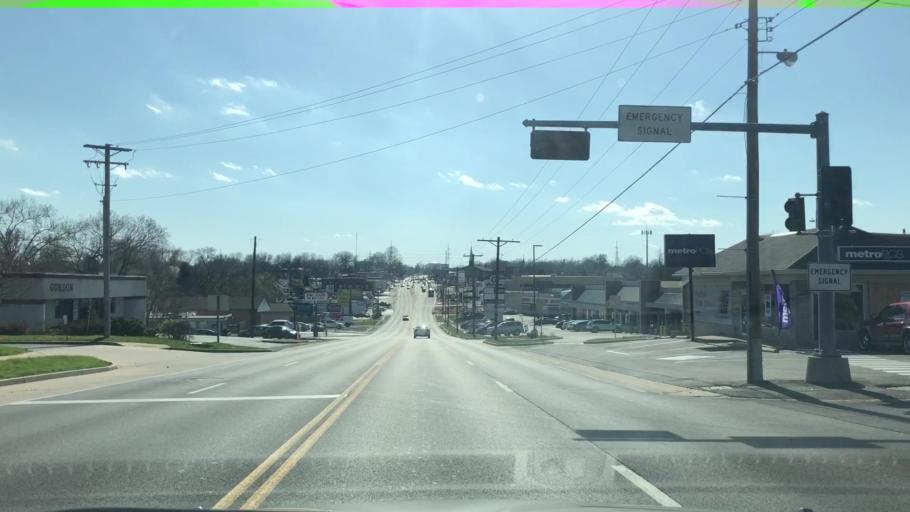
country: US
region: Missouri
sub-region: Saint Louis County
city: Affton
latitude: 38.5542
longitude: -90.3180
